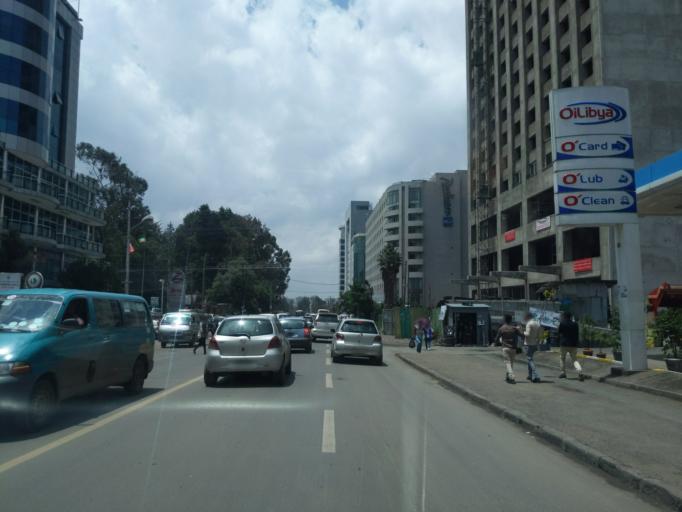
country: ET
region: Adis Abeba
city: Addis Ababa
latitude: 9.0167
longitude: 38.7662
